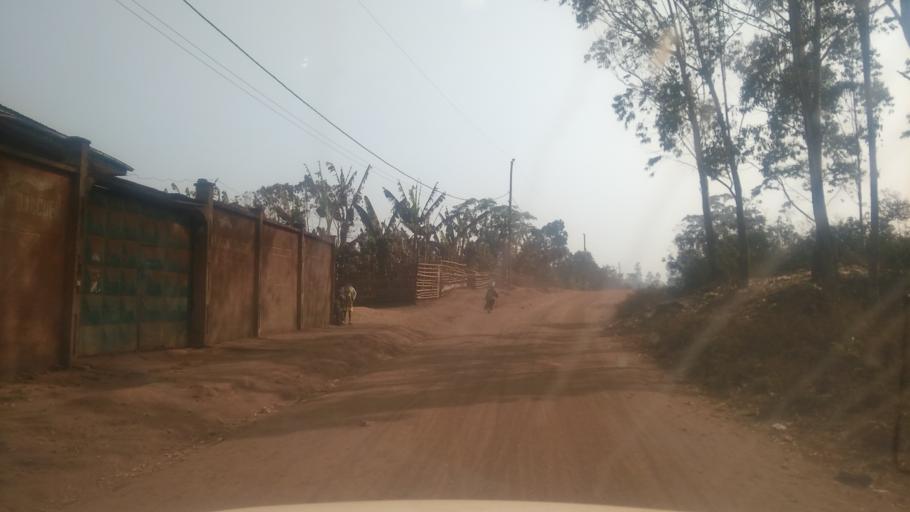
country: CM
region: West
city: Bafoussam
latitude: 5.5139
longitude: 10.4069
